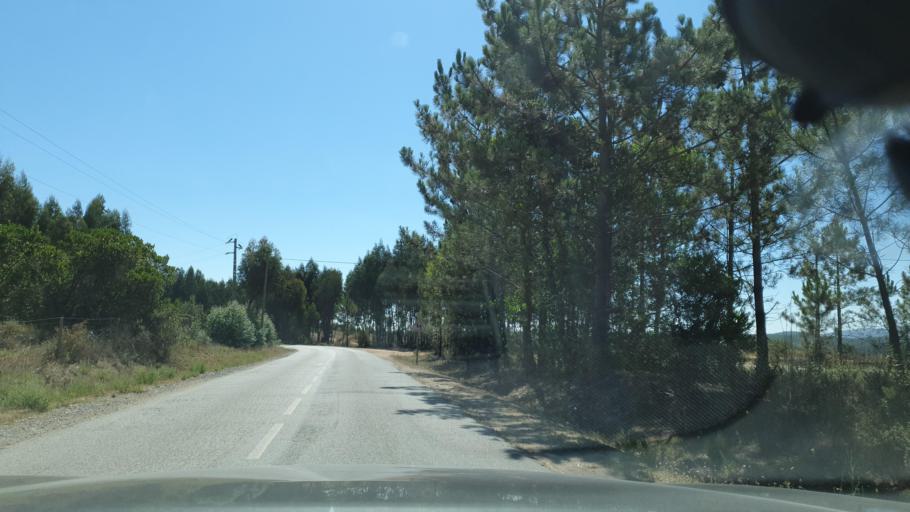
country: PT
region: Beja
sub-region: Odemira
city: Sao Teotonio
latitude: 37.4983
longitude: -8.6666
